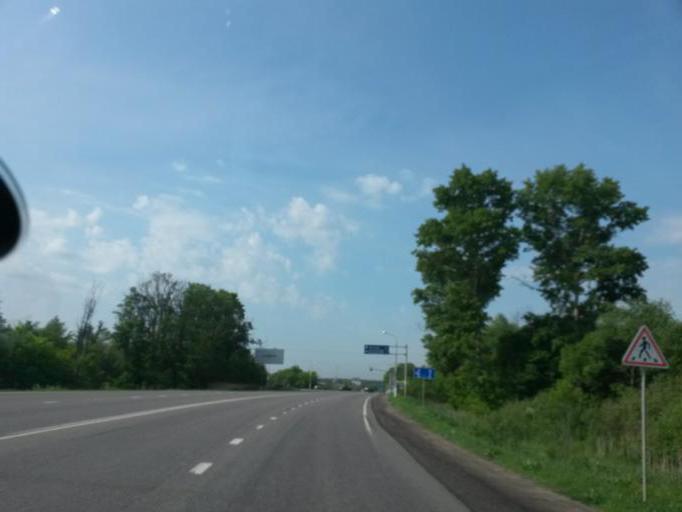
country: RU
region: Moskovskaya
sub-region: Chekhovskiy Rayon
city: Chekhov
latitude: 55.1897
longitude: 37.5015
